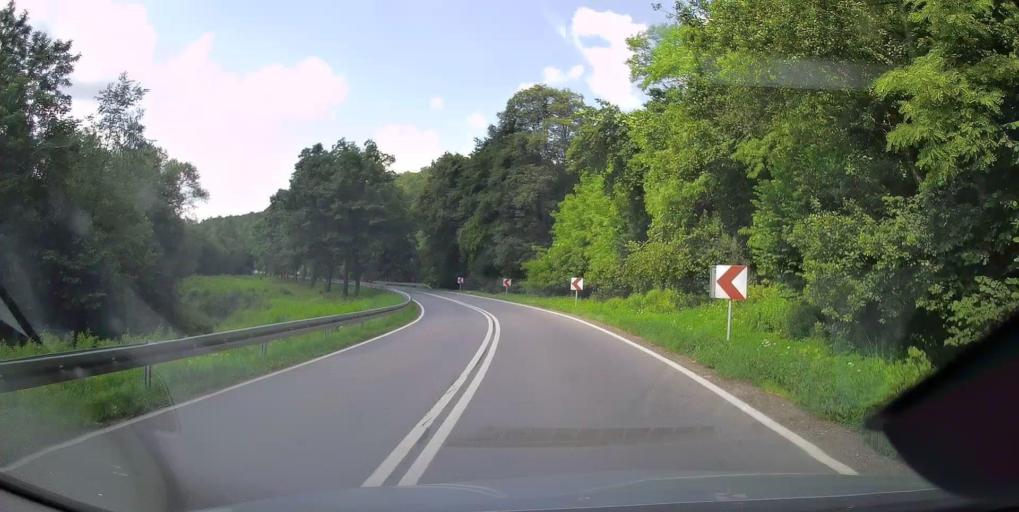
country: PL
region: Lesser Poland Voivodeship
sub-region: Powiat tarnowski
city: Zakliczyn
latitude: 49.8297
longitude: 20.8092
